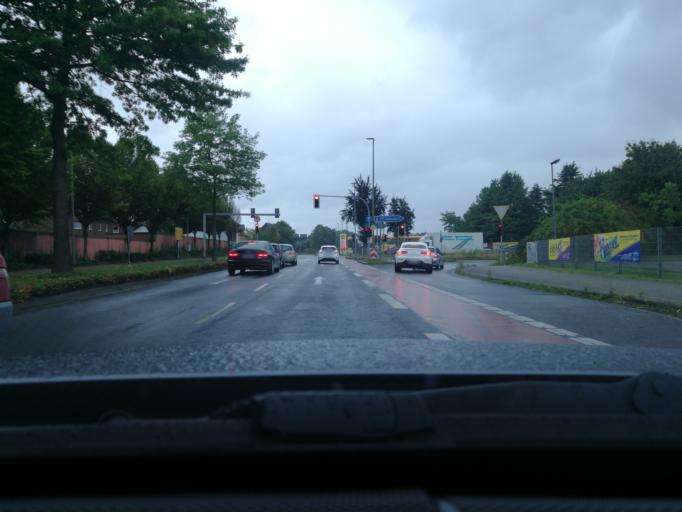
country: DE
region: North Rhine-Westphalia
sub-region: Regierungsbezirk Dusseldorf
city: Dinslaken
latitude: 51.5441
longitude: 6.7328
